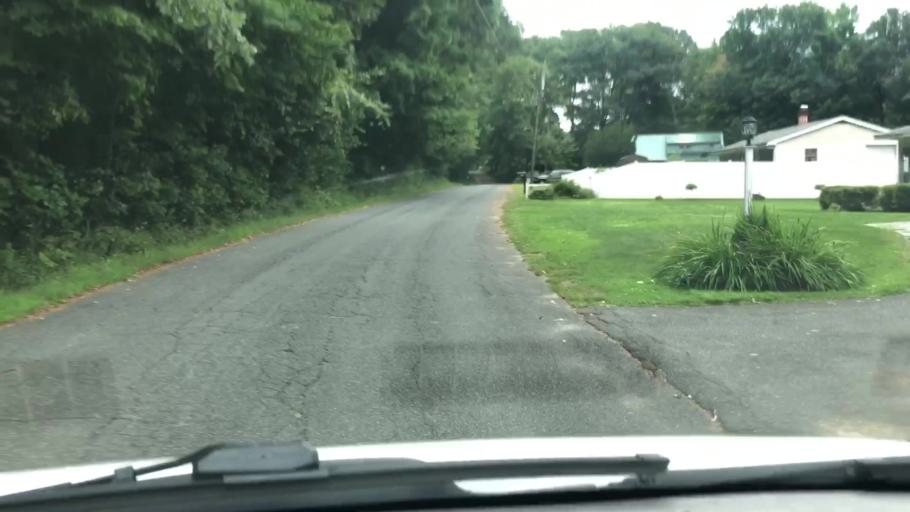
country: US
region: Massachusetts
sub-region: Franklin County
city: Greenfield
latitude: 42.5332
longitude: -72.5987
